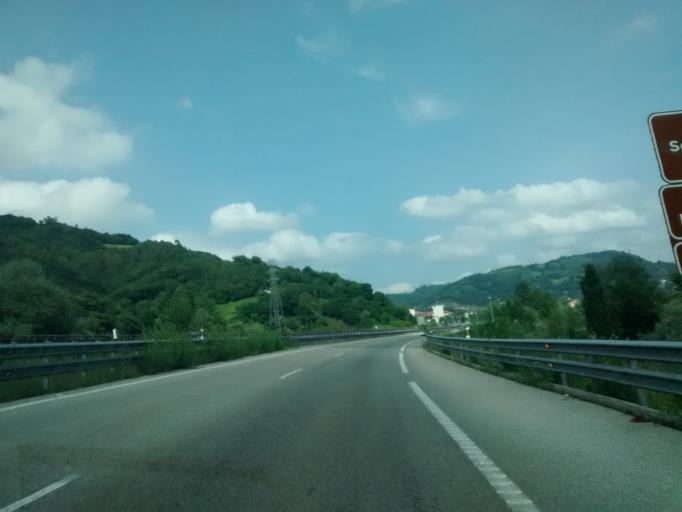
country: ES
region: Asturias
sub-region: Province of Asturias
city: Sama
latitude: 43.3214
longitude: -5.7420
